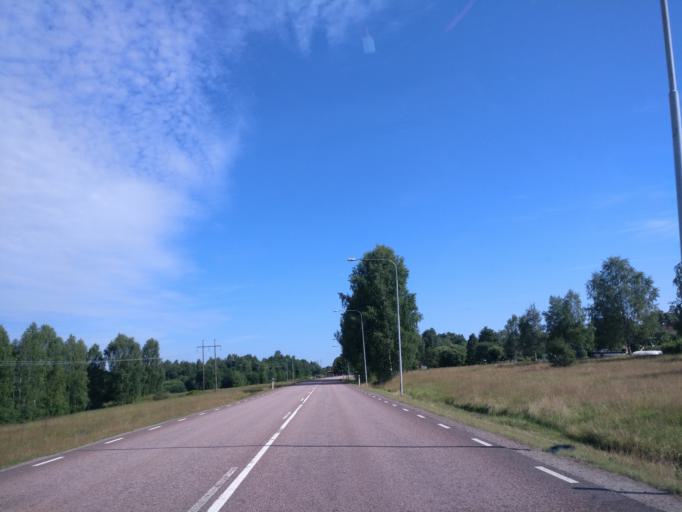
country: SE
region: Vaermland
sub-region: Hagfors Kommun
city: Hagfors
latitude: 60.0519
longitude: 13.7045
